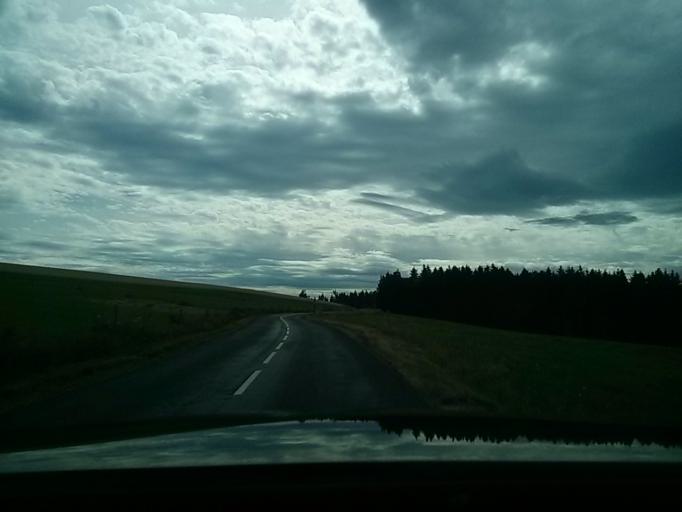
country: FR
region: Rhone-Alpes
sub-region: Departement de la Loire
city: Saint-Genest-Malifaux
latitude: 45.3589
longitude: 4.4741
